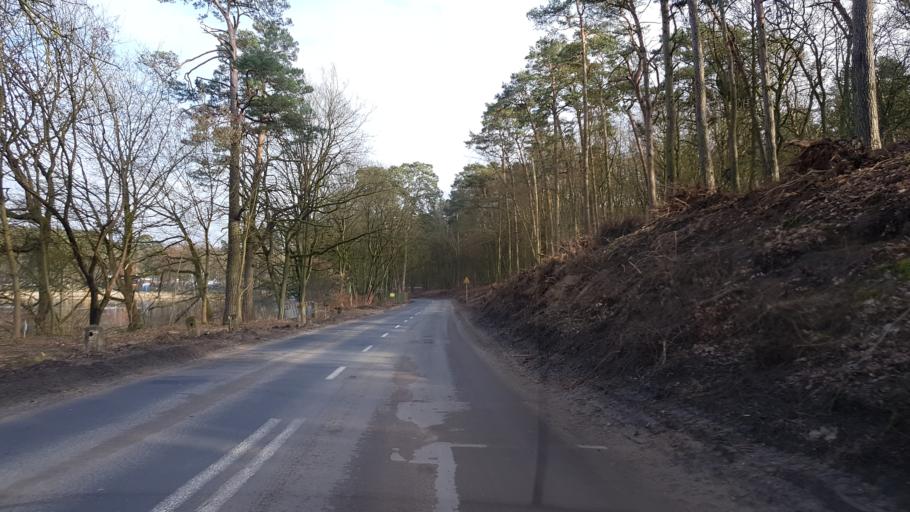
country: PL
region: West Pomeranian Voivodeship
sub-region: Szczecin
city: Szczecin
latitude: 53.4717
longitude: 14.4799
